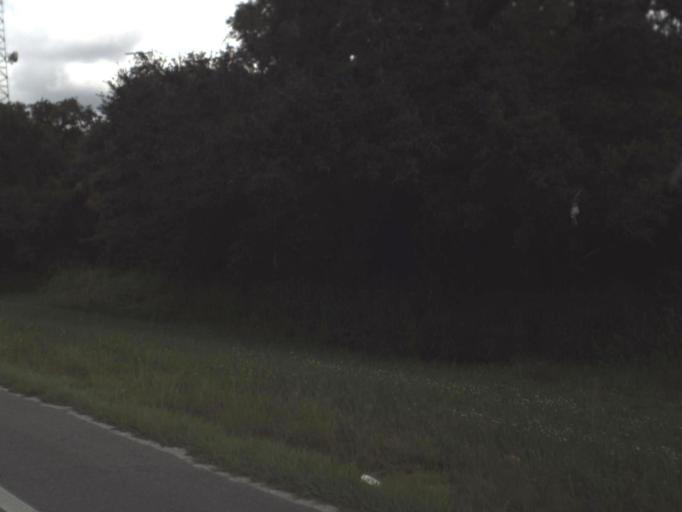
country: US
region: Florida
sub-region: Hendry County
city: LaBelle
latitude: 26.7732
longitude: -81.4374
